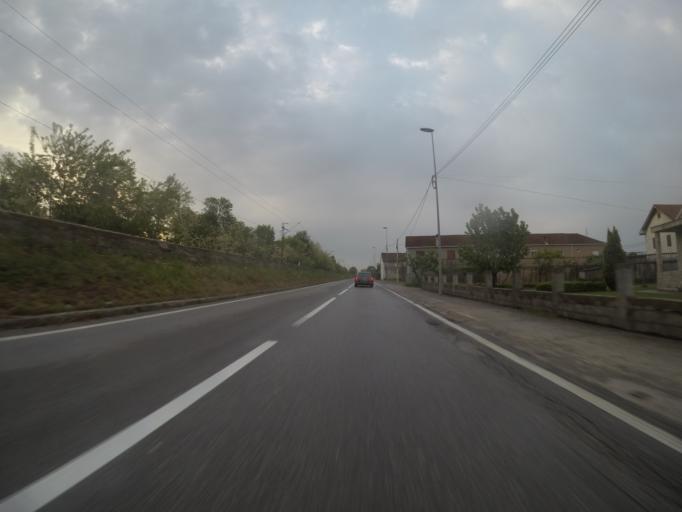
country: ME
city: Mojanovici
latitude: 42.3054
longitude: 19.1872
